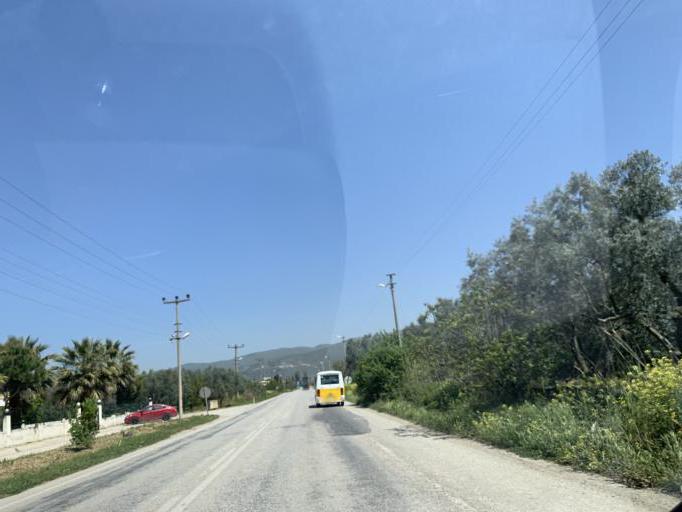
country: TR
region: Bursa
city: Iznik
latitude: 40.4153
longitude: 29.7127
